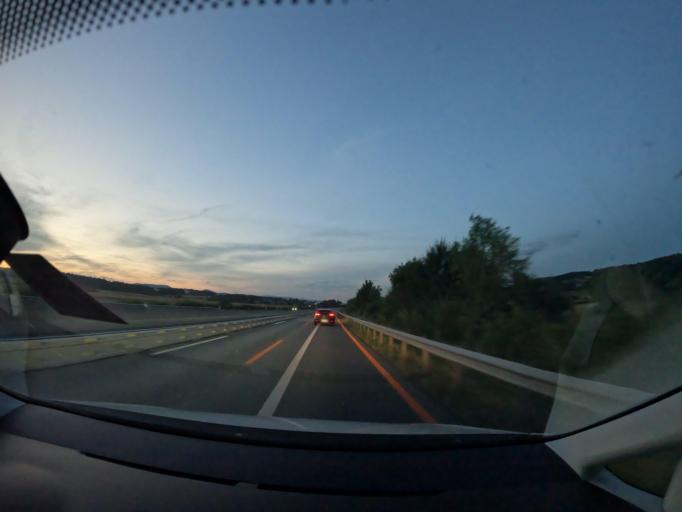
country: AT
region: Styria
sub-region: Politischer Bezirk Hartberg-Fuerstenfeld
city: Sebersdorf
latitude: 47.2077
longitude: 15.9883
